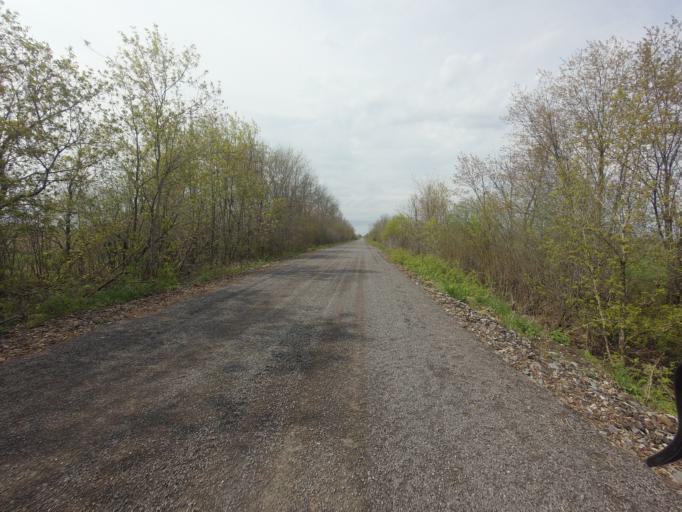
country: CA
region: Ontario
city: Carleton Place
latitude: 45.1678
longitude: -76.1496
